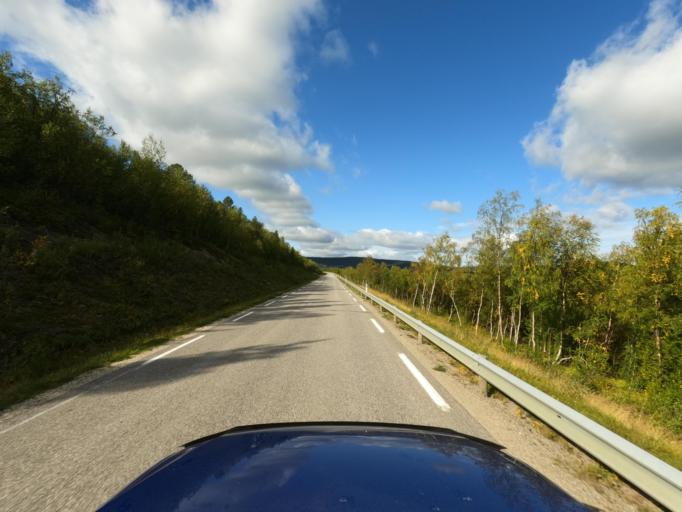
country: NO
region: Finnmark Fylke
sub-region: Karasjok
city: Karasjohka
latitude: 69.4551
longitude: 25.5687
